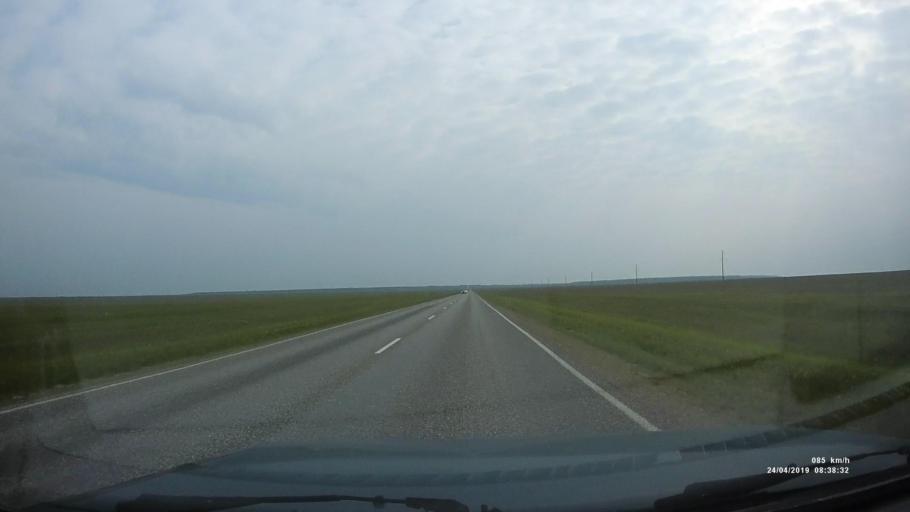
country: RU
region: Kalmykiya
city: Arshan'
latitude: 46.2159
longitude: 43.9688
